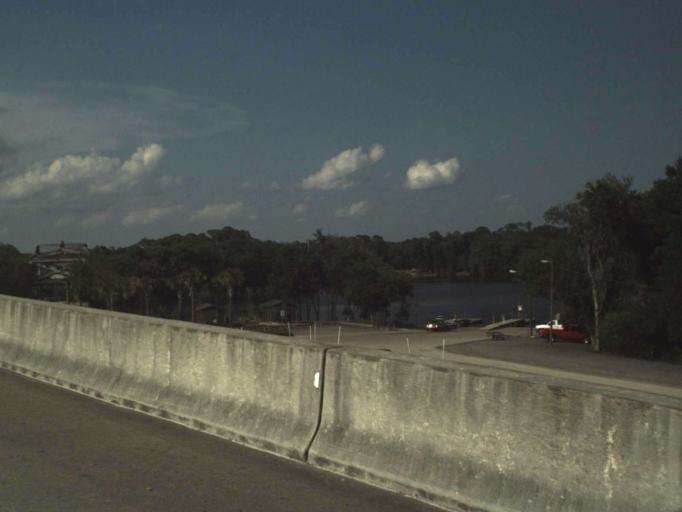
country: US
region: Florida
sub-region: Volusia County
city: DeBary
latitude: 28.8356
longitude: -81.3245
